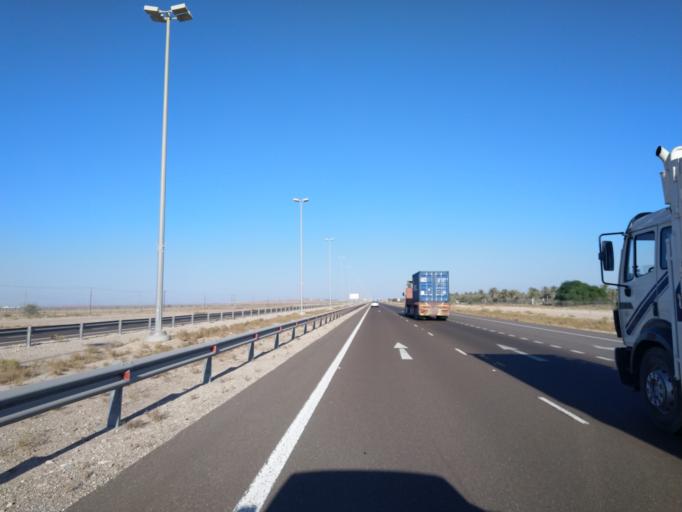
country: OM
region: Al Buraimi
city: Al Buraymi
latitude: 24.4868
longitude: 55.3923
